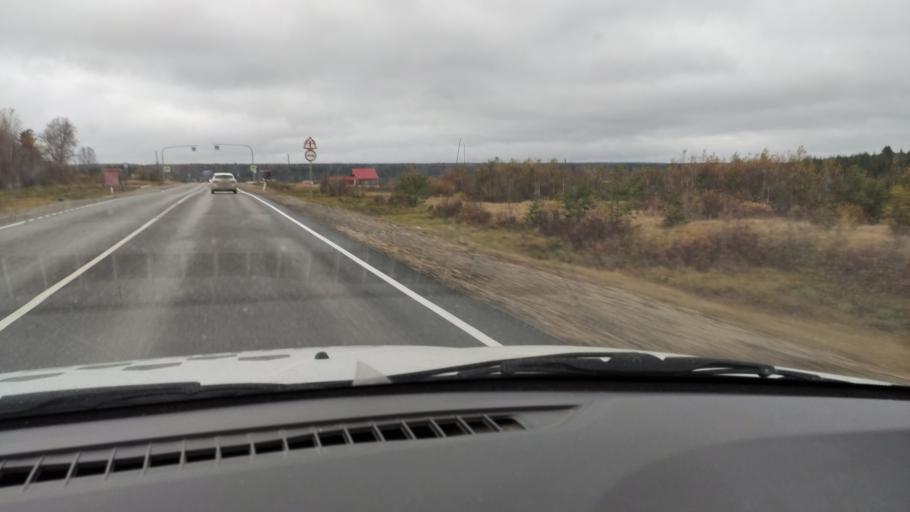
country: RU
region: Kirov
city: Chernaya Kholunitsa
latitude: 58.8583
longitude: 51.7103
